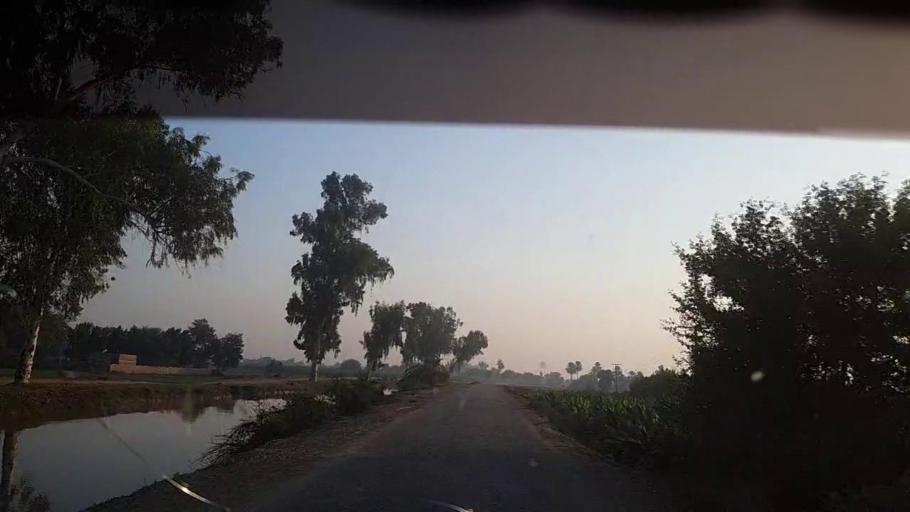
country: PK
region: Sindh
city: Ranipur
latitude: 27.2368
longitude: 68.5493
